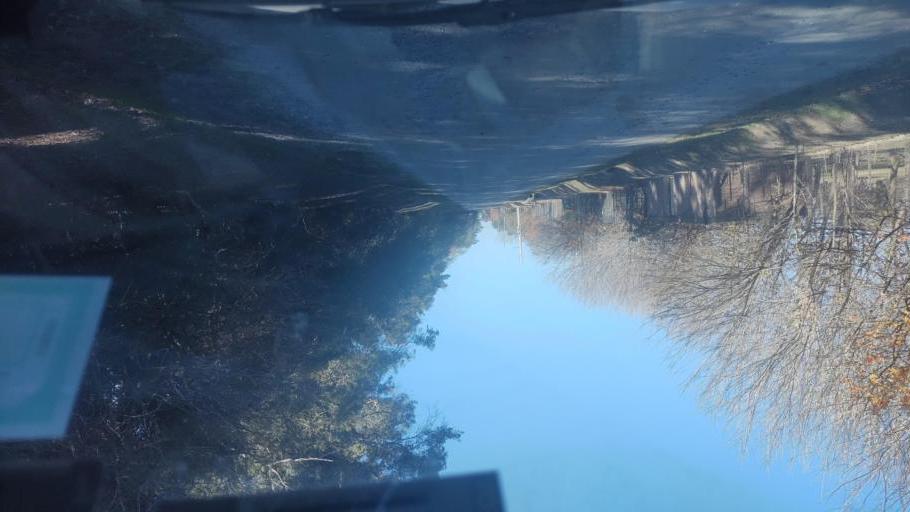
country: AR
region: Buenos Aires
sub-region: Partido de La Plata
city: La Plata
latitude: -34.8543
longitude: -58.1074
